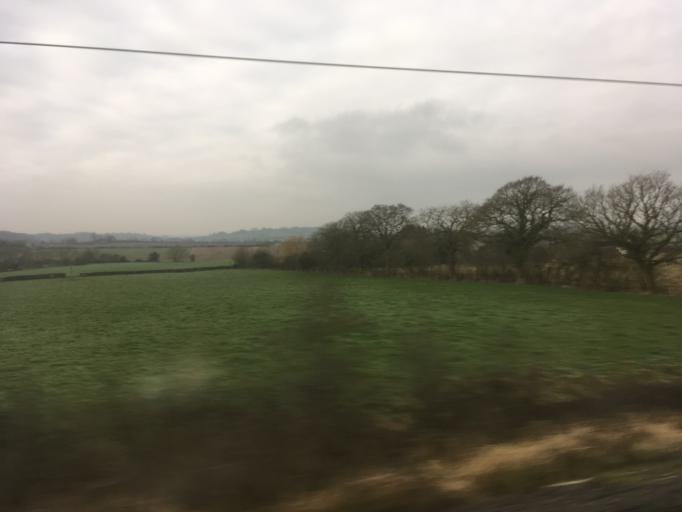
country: GB
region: England
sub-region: Wiltshire
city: Royal Wootton Bassett
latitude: 51.5453
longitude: -1.9232
